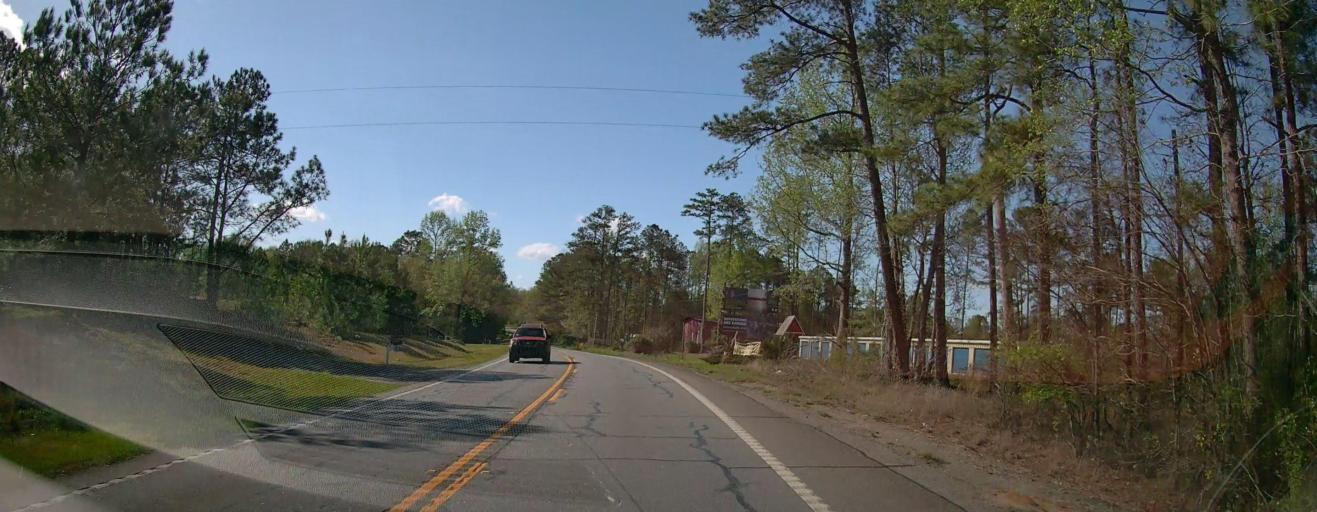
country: US
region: Georgia
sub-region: Baldwin County
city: Hardwick
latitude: 33.0885
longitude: -83.1737
